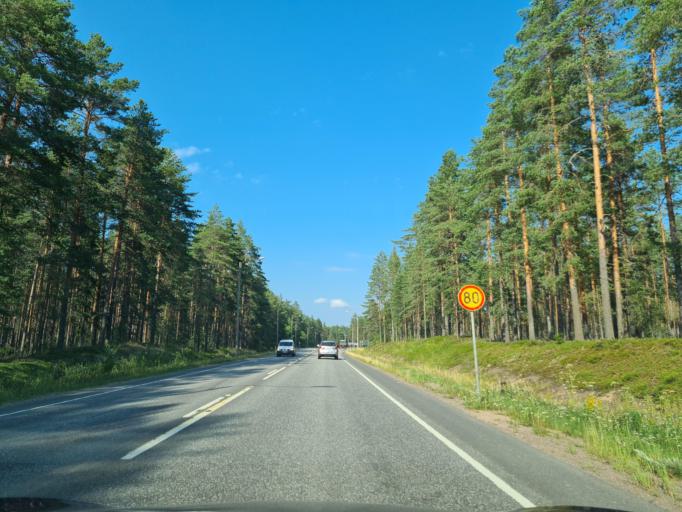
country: FI
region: Satakunta
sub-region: Pohjois-Satakunta
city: Kankaanpaeae
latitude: 61.8450
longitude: 22.4564
